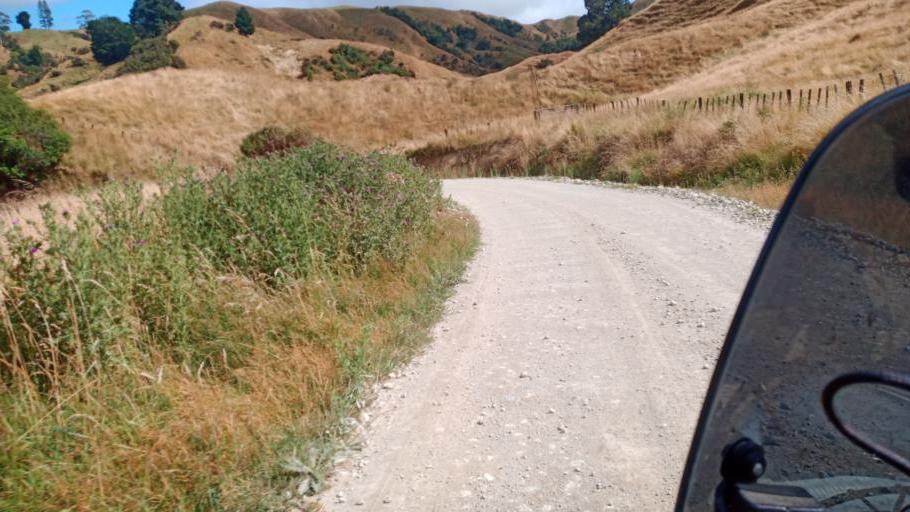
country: NZ
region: Hawke's Bay
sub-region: Wairoa District
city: Wairoa
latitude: -38.6092
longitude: 177.4407
